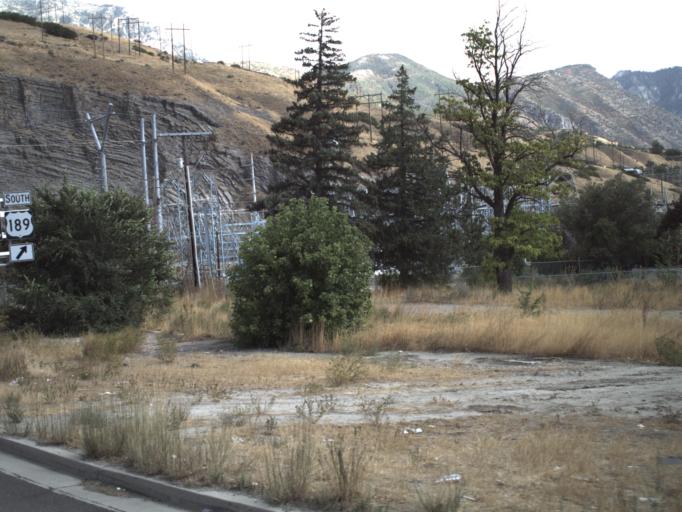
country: US
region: Utah
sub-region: Utah County
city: Orem
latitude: 40.3128
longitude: -111.6612
